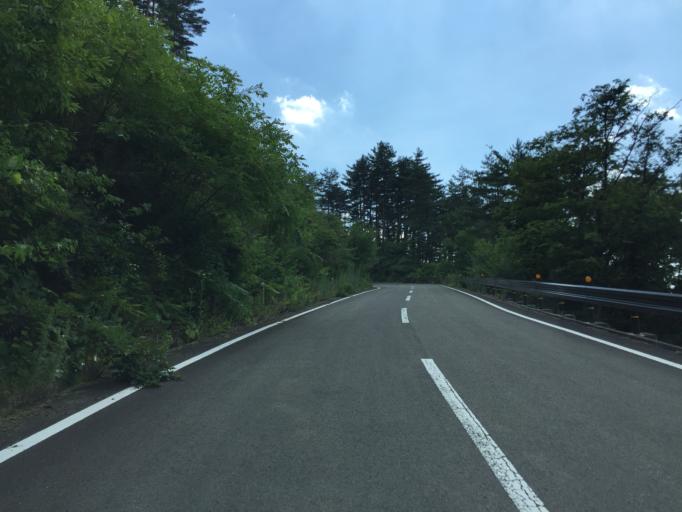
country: JP
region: Fukushima
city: Yanagawamachi-saiwaicho
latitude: 37.7641
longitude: 140.6783
